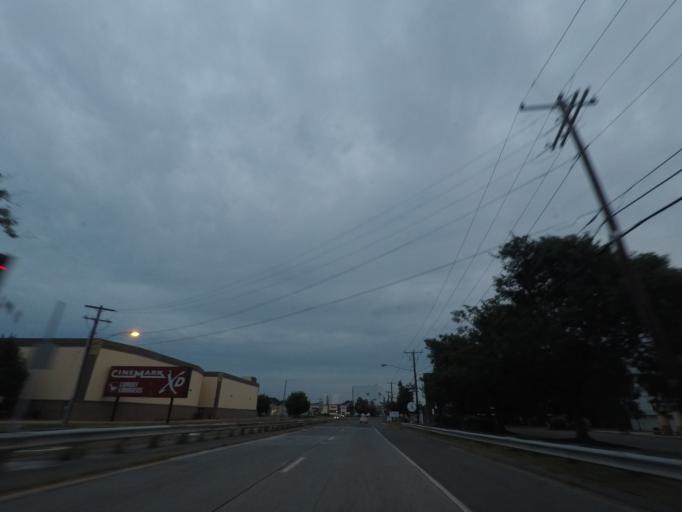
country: US
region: Massachusetts
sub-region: Hampden County
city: West Springfield
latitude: 42.1268
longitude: -72.6263
